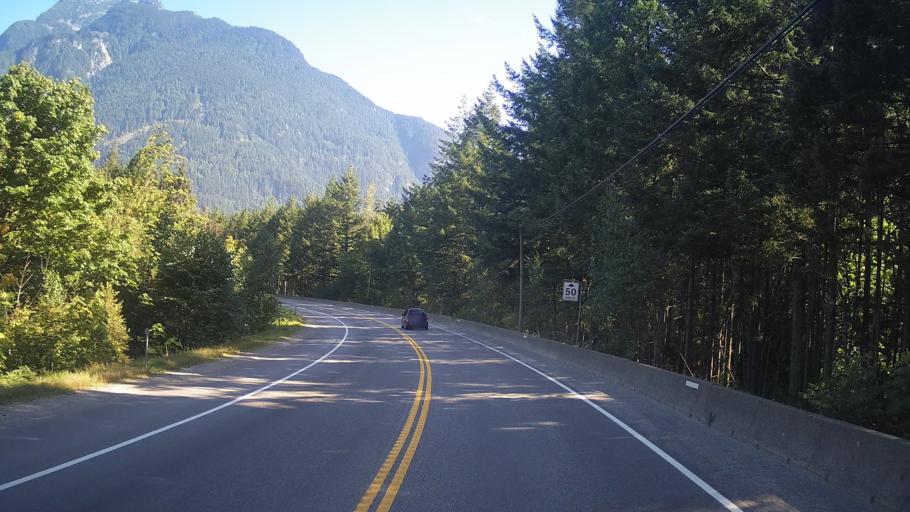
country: CA
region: British Columbia
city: Hope
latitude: 49.3886
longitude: -121.4613
